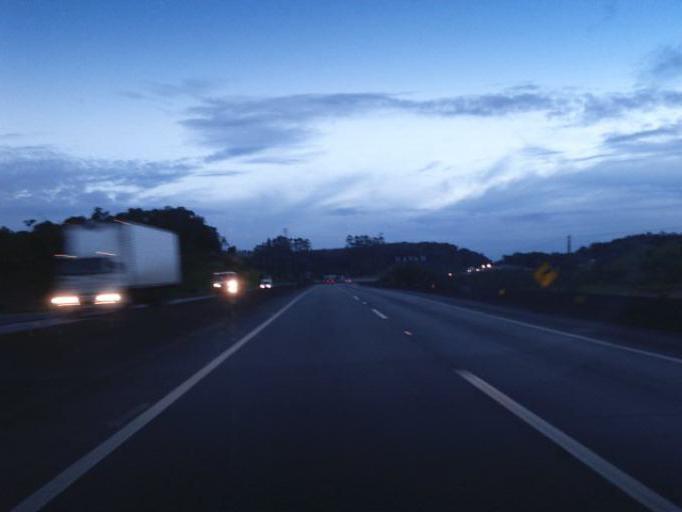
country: BR
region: Santa Catarina
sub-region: Joinville
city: Joinville
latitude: -26.3932
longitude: -48.8393
